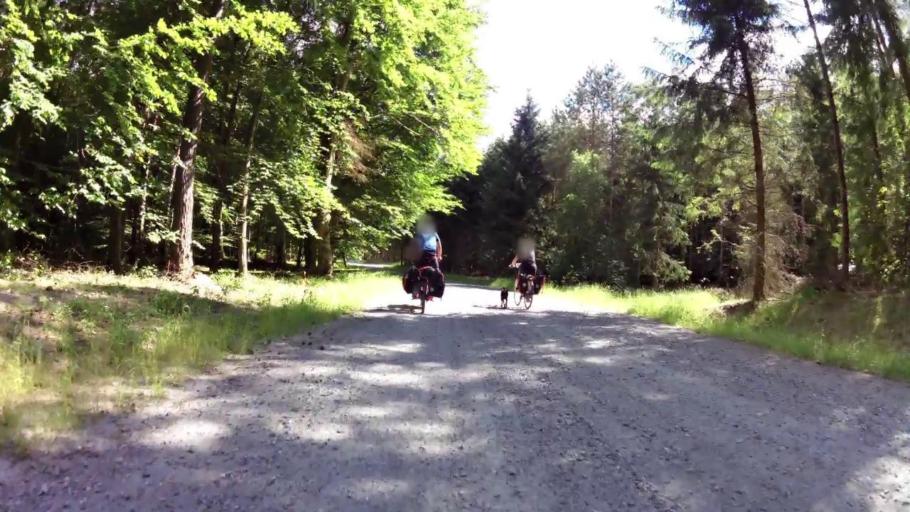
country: PL
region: West Pomeranian Voivodeship
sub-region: Powiat lobeski
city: Lobez
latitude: 53.6799
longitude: 15.5513
